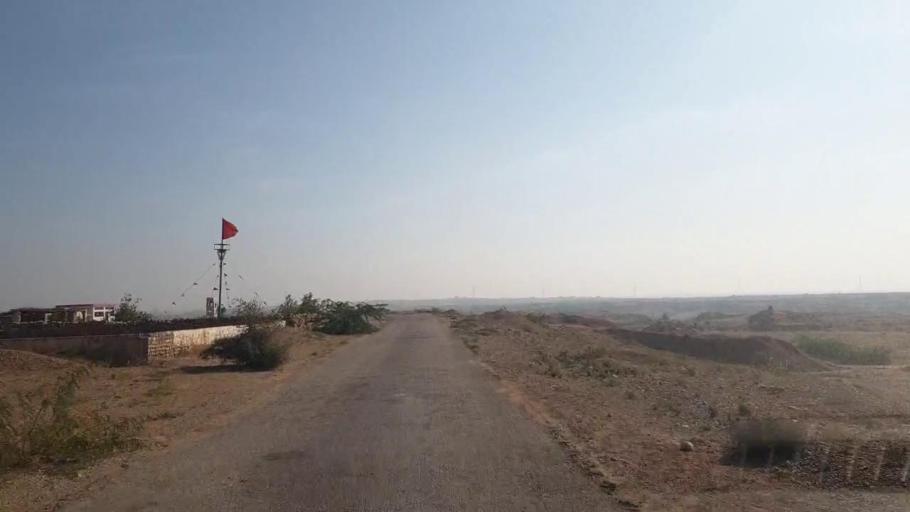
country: PK
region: Sindh
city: Matiari
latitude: 25.6225
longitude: 68.3143
